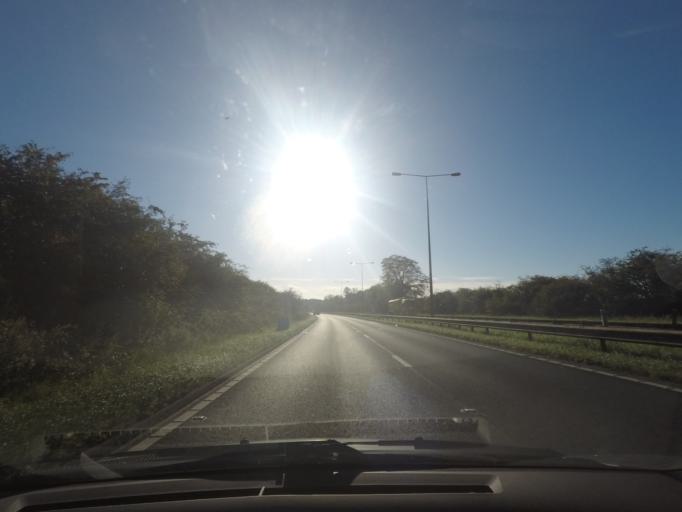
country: GB
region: England
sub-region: East Riding of Yorkshire
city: Welton
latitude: 53.7360
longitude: -0.5603
